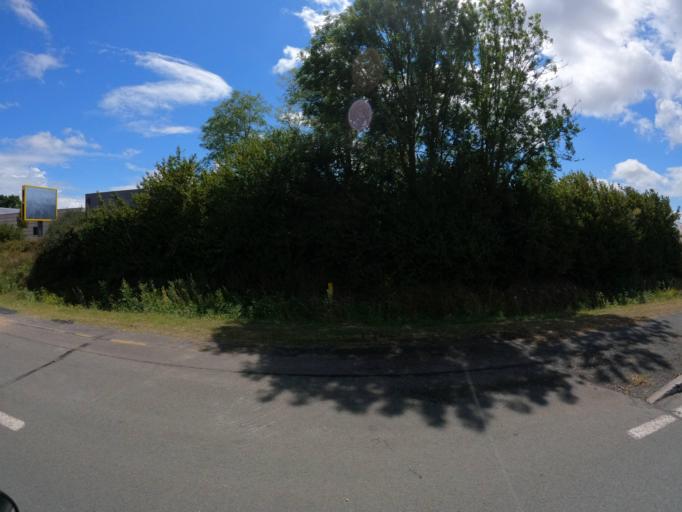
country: FR
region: Pays de la Loire
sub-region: Departement de Maine-et-Loire
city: Avrille
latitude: 47.5185
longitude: -0.6134
